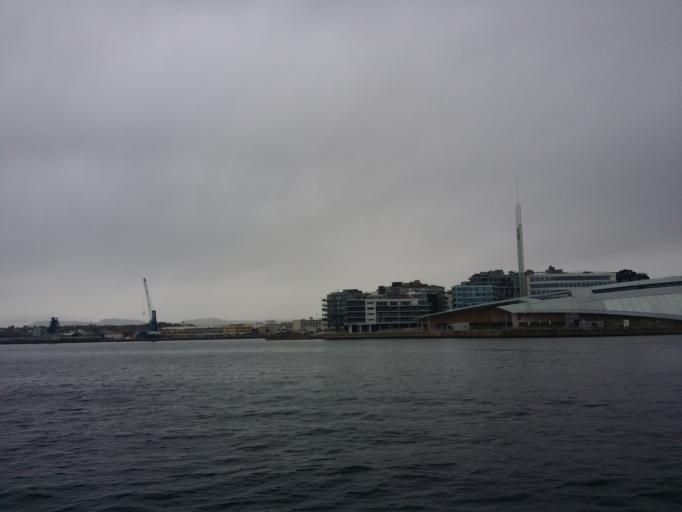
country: NO
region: Oslo
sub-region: Oslo
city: Oslo
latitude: 59.9046
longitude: 10.7247
